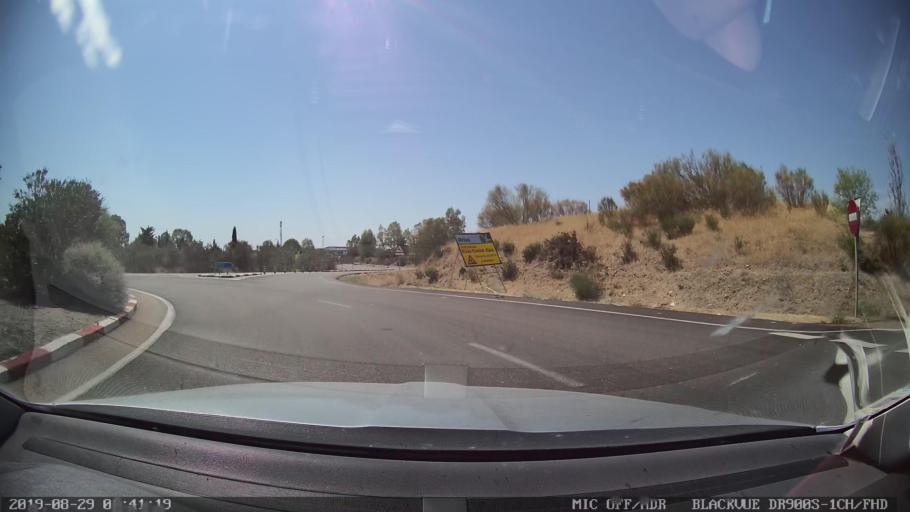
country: ES
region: Extremadura
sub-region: Provincia de Badajoz
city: Badajoz
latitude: 38.8867
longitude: -7.0265
